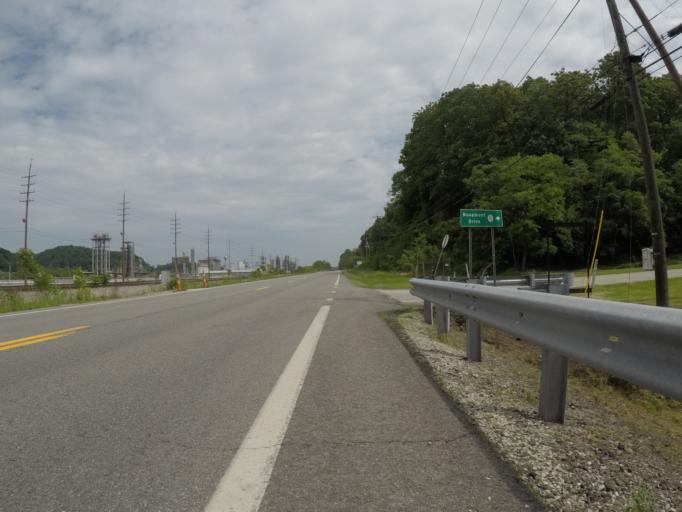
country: US
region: West Virginia
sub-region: Wayne County
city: Kenova
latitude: 38.3499
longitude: -82.5934
